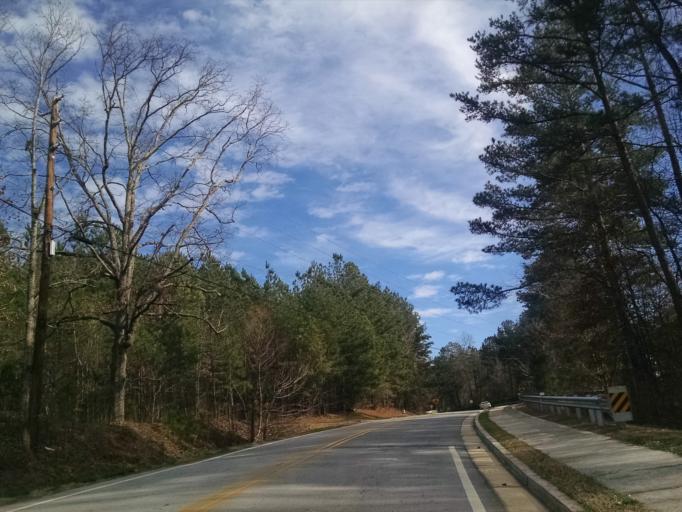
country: US
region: Georgia
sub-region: Gwinnett County
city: Sugar Hill
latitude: 34.1227
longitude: -84.0639
